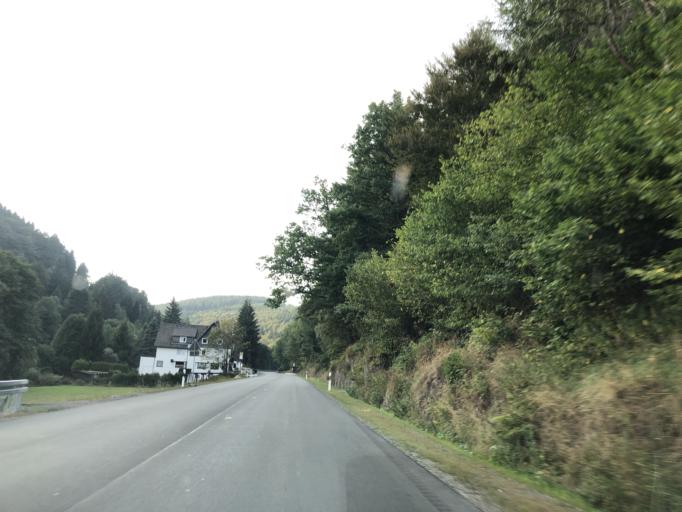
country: DE
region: North Rhine-Westphalia
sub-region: Regierungsbezirk Arnsberg
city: Winterberg
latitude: 51.1627
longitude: 8.5579
